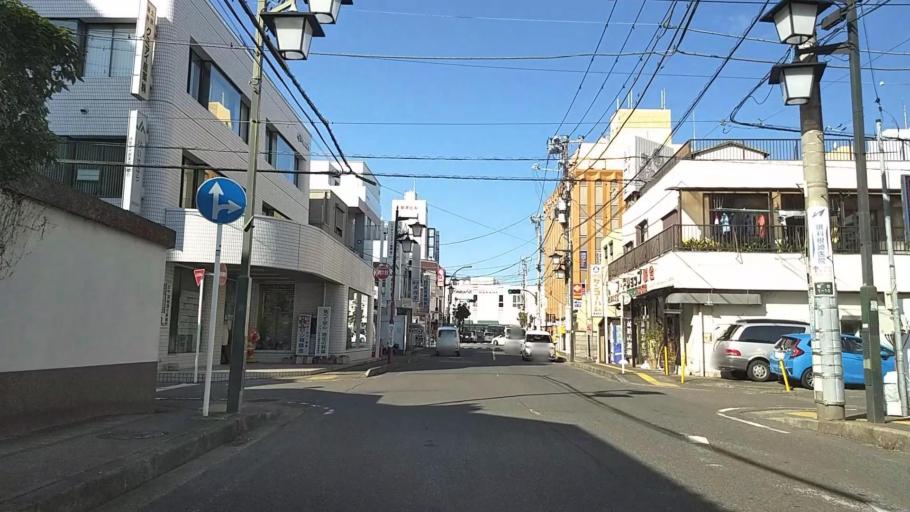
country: JP
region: Kanagawa
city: Isehara
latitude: 35.3944
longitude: 139.3144
